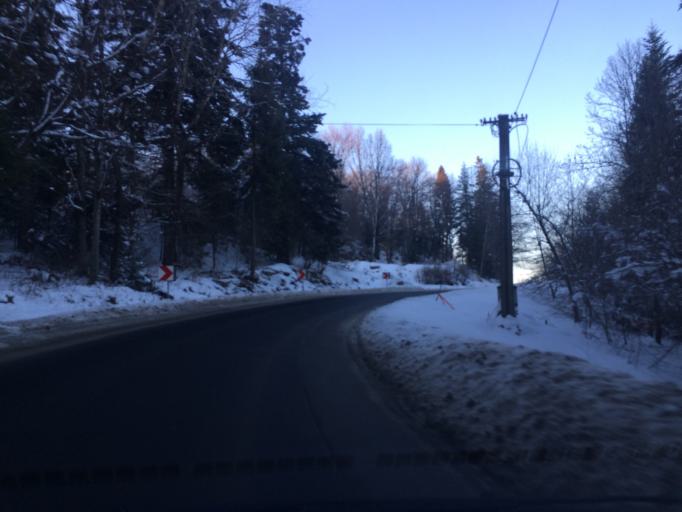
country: PL
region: Subcarpathian Voivodeship
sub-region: Powiat bieszczadzki
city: Lutowiska
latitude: 49.2731
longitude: 22.6861
